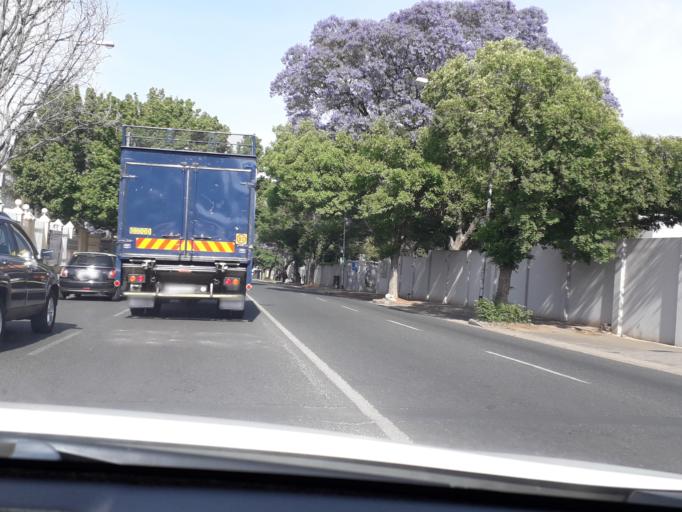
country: ZA
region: Gauteng
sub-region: City of Johannesburg Metropolitan Municipality
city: Johannesburg
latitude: -26.1263
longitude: 28.0829
